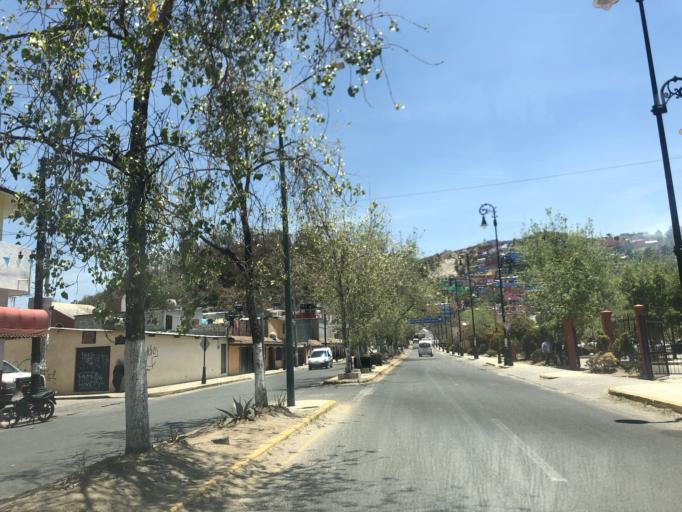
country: MX
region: Chiapas
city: San Cristobal de las Casas
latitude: 16.7211
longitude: -92.6360
